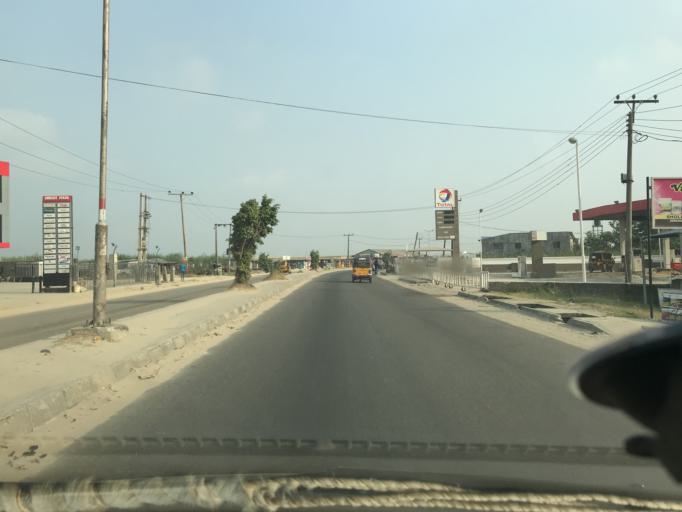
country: NG
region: Lagos
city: Ikoyi
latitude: 6.4763
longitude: 3.5682
